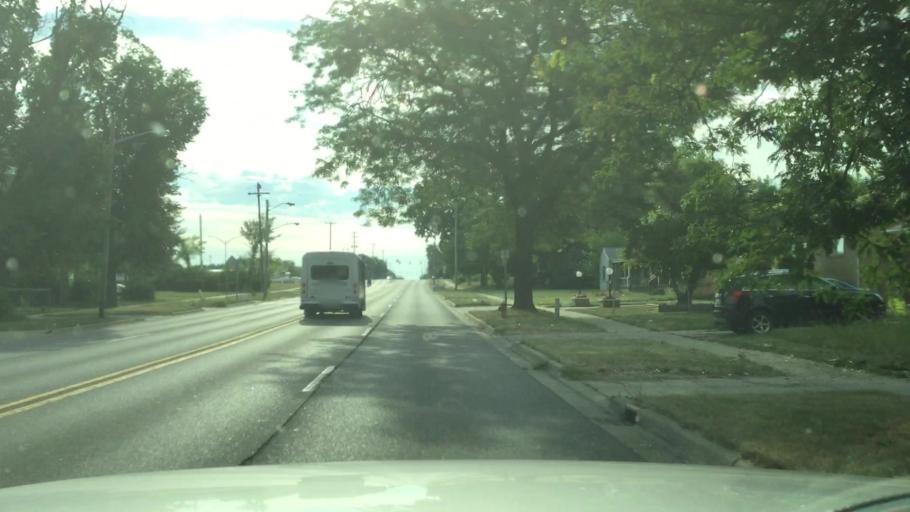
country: US
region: Michigan
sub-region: Genesee County
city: Beecher
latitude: 43.0610
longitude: -83.7085
